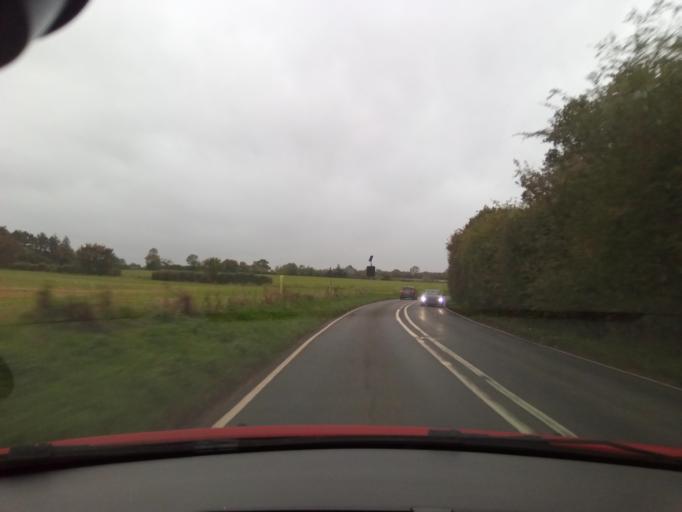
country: GB
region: England
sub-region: Suffolk
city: Kedington
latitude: 52.0546
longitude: 0.5058
